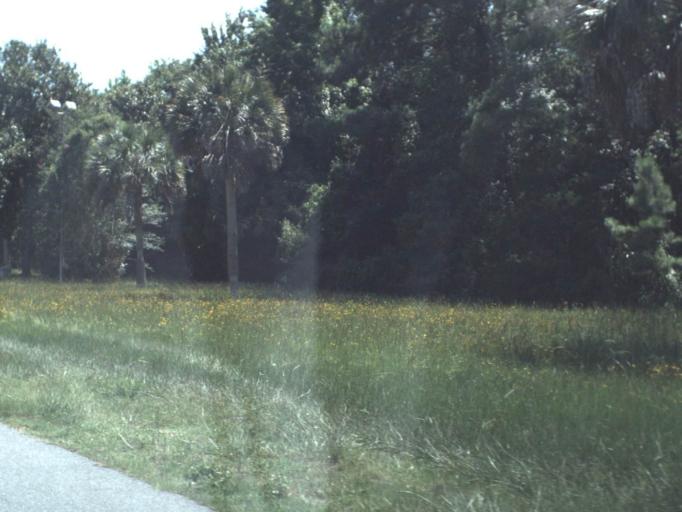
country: US
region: Georgia
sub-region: Camden County
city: Kingsland
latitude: 30.7394
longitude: -81.6881
